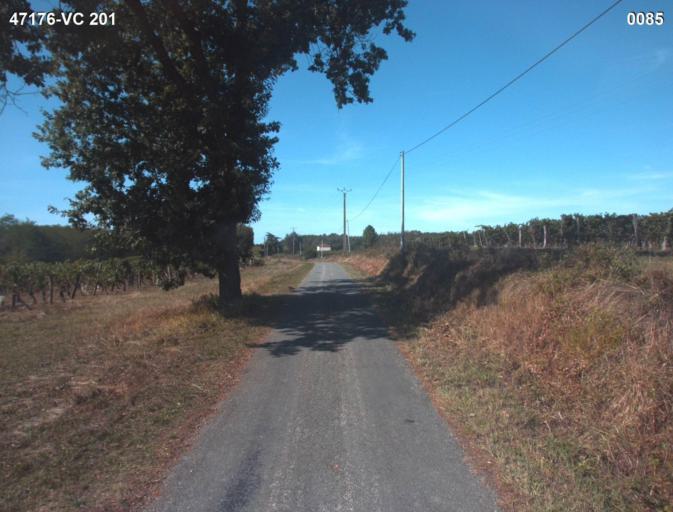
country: FR
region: Aquitaine
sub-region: Departement du Lot-et-Garonne
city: Vianne
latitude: 44.2095
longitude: 0.3124
